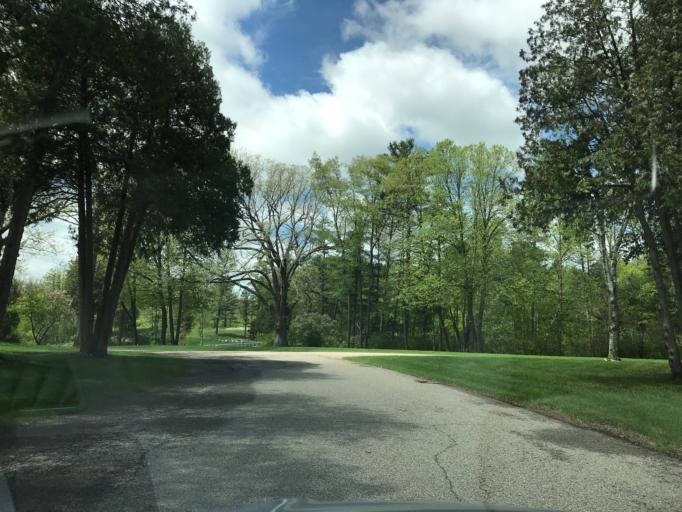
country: US
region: Michigan
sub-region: Oakland County
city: Franklin
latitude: 42.4734
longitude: -83.2996
